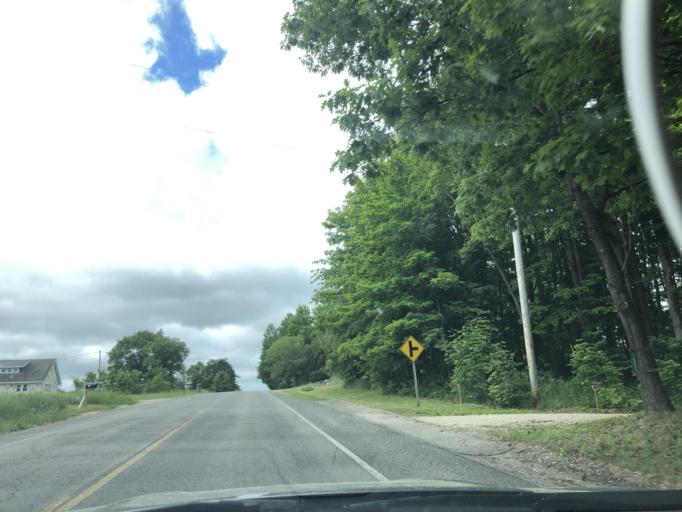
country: US
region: Michigan
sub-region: Missaukee County
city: Lake City
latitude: 44.4493
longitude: -85.2163
